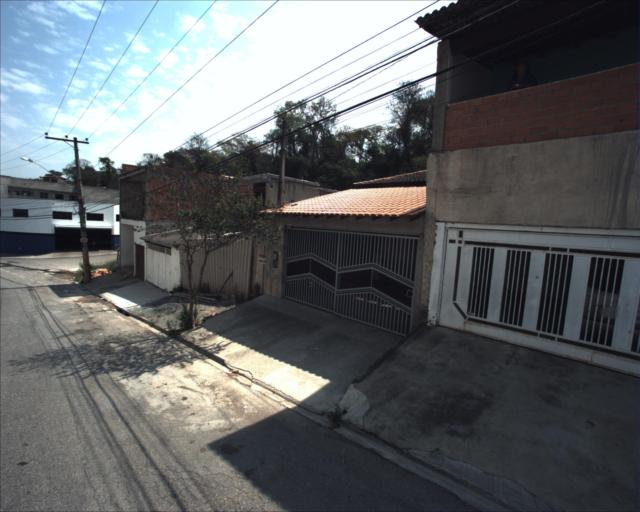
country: BR
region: Sao Paulo
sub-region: Sorocaba
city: Sorocaba
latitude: -23.4390
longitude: -47.4805
